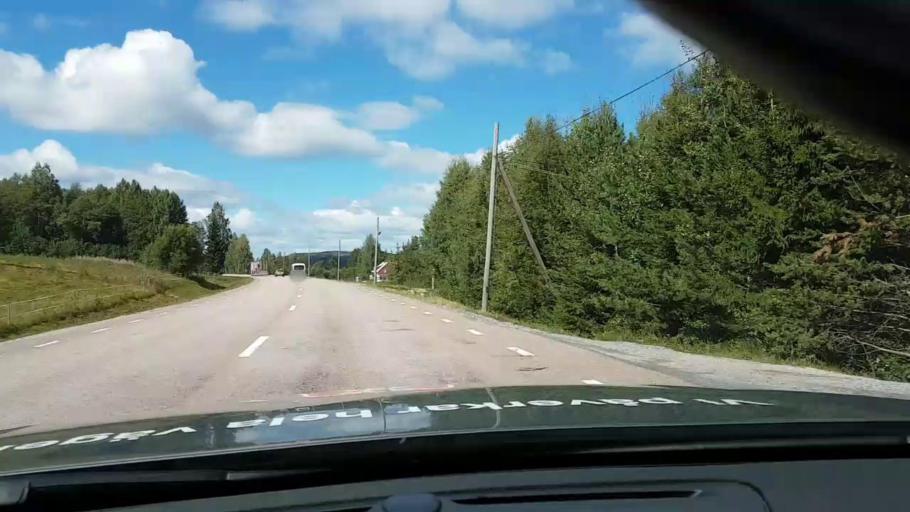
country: SE
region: Vaesternorrland
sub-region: OErnskoeldsviks Kommun
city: Bjasta
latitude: 63.3563
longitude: 18.4834
